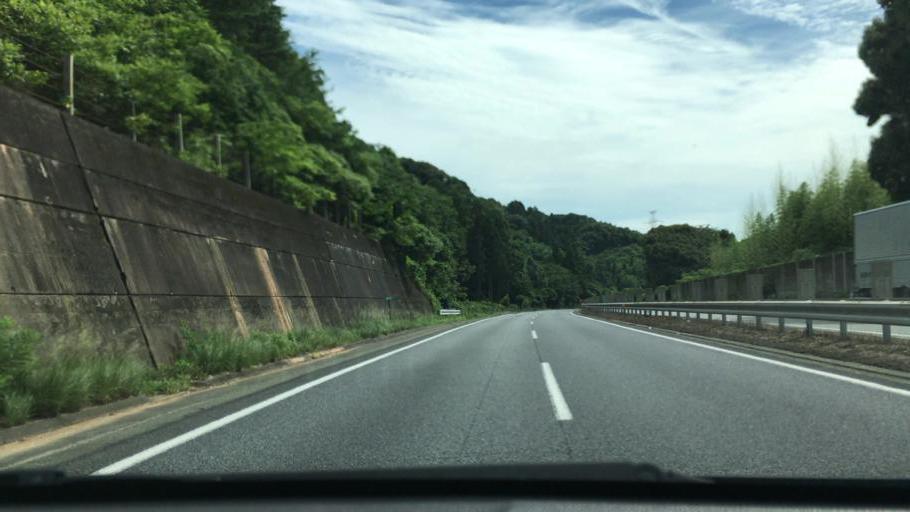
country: JP
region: Yamaguchi
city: Ogori-shimogo
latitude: 34.1262
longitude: 131.4203
